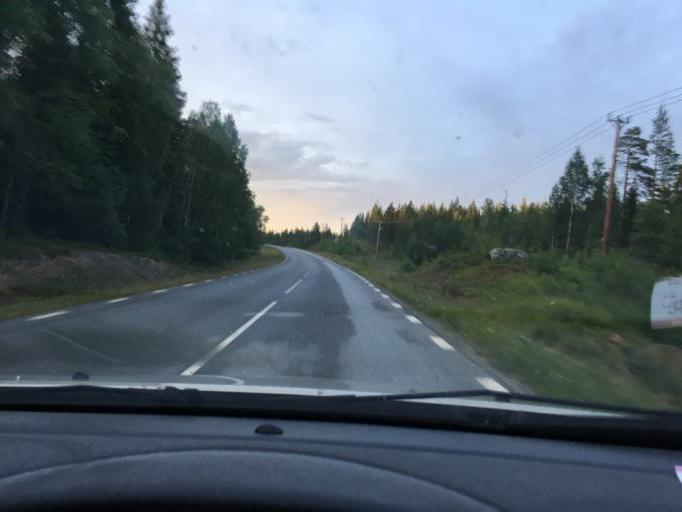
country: SE
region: Norrbotten
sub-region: Kalix Kommun
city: Toere
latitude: 66.0547
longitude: 22.5908
